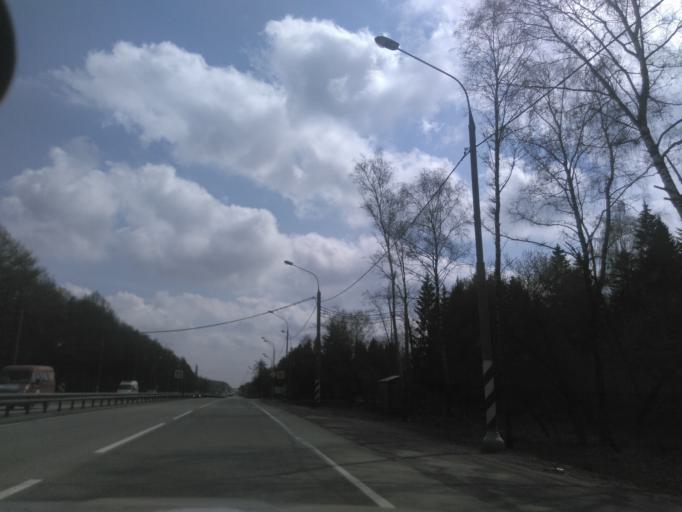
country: RU
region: Moskovskaya
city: Mendeleyevo
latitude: 56.0196
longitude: 37.1939
